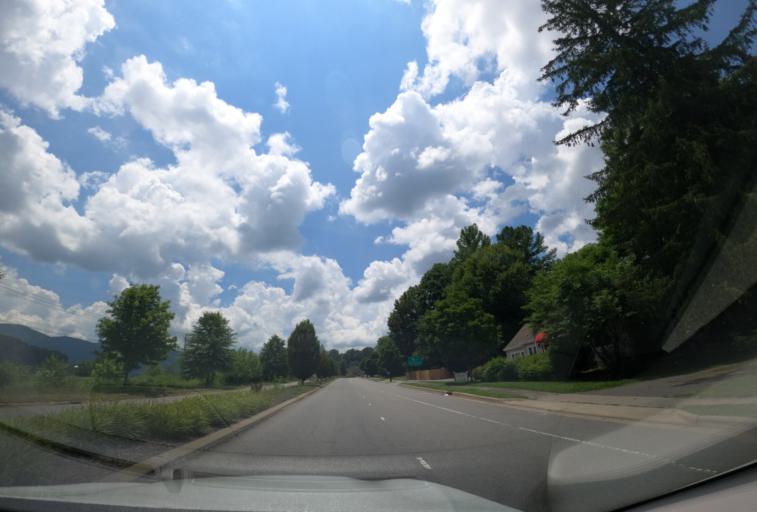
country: US
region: North Carolina
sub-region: Haywood County
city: Waynesville
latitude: 35.5005
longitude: -82.9654
